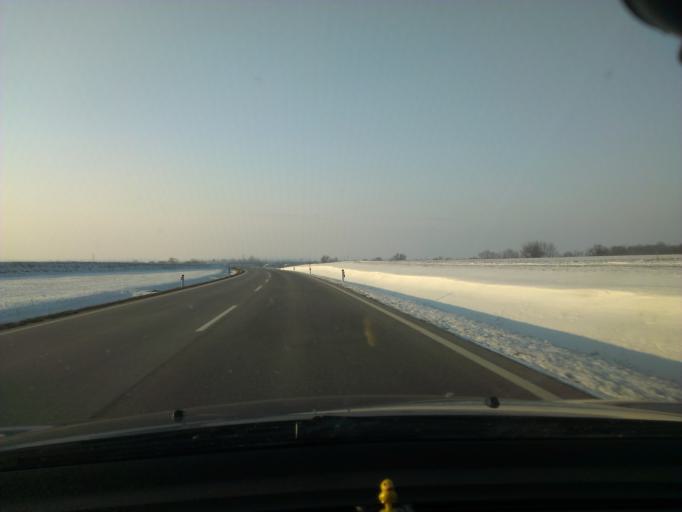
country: AT
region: Burgenland
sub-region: Eisenstadt-Umgebung
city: Schutzen am Gebirge
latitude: 47.8539
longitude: 16.6056
